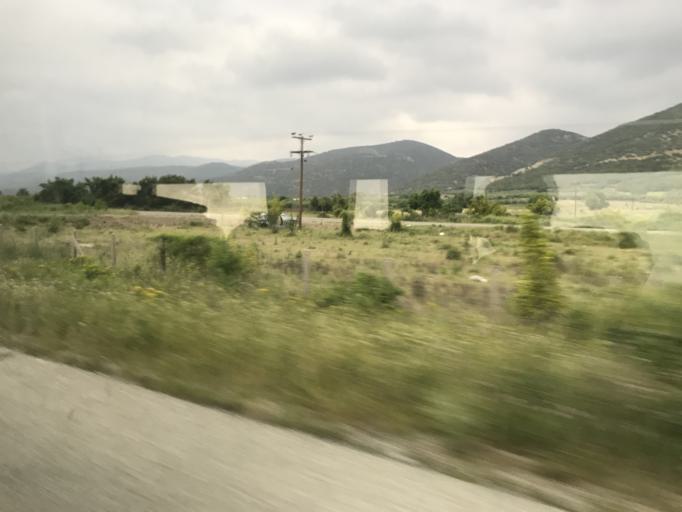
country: GR
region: East Macedonia and Thrace
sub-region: Nomos Xanthis
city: Selero
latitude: 41.1201
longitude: 25.0859
